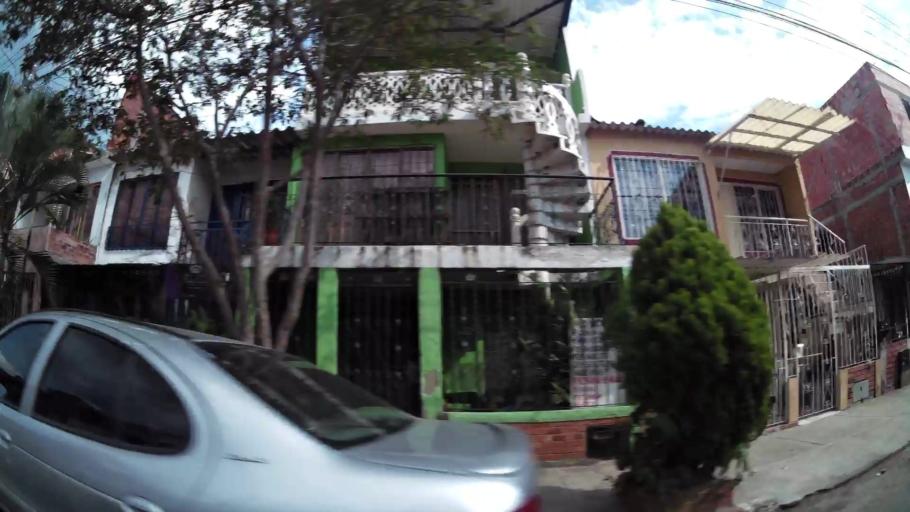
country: CO
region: Valle del Cauca
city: Cali
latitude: 3.3962
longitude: -76.5052
